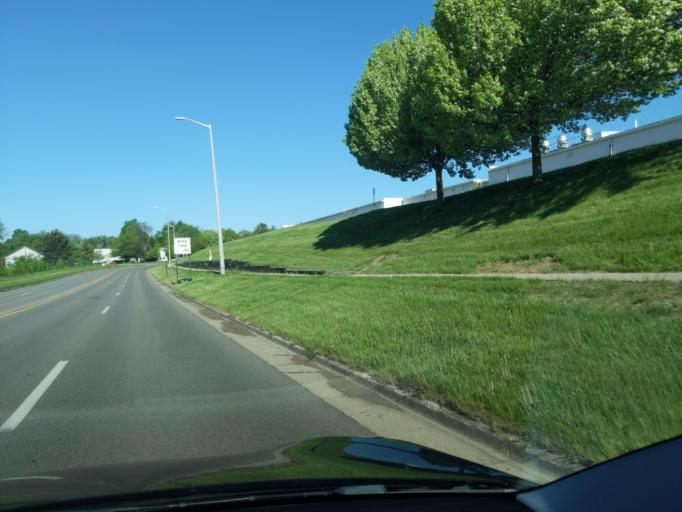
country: US
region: Michigan
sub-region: Kent County
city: East Grand Rapids
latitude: 42.9102
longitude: -85.5638
